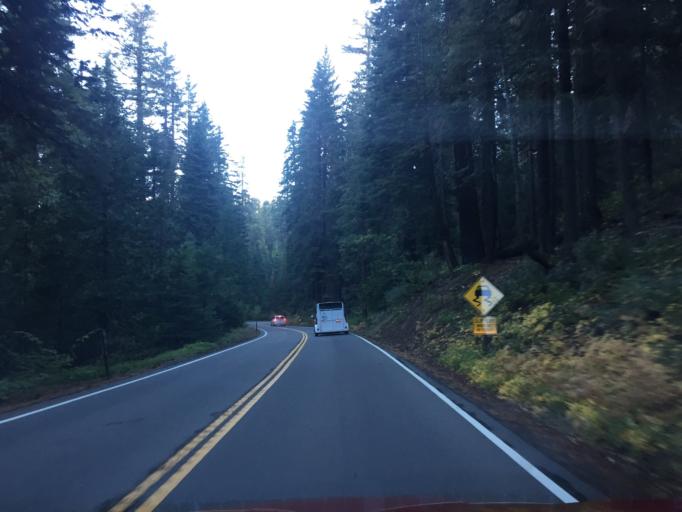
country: US
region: California
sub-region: Mariposa County
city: Yosemite Valley
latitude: 37.6487
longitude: -119.7023
